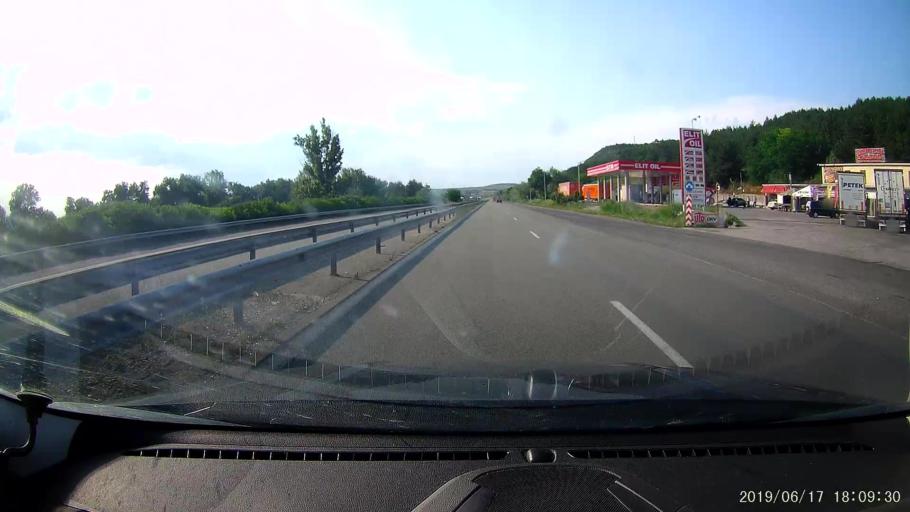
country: BG
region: Khaskovo
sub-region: Obshtina Lyubimets
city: Lyubimets
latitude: 41.8601
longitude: 26.0889
